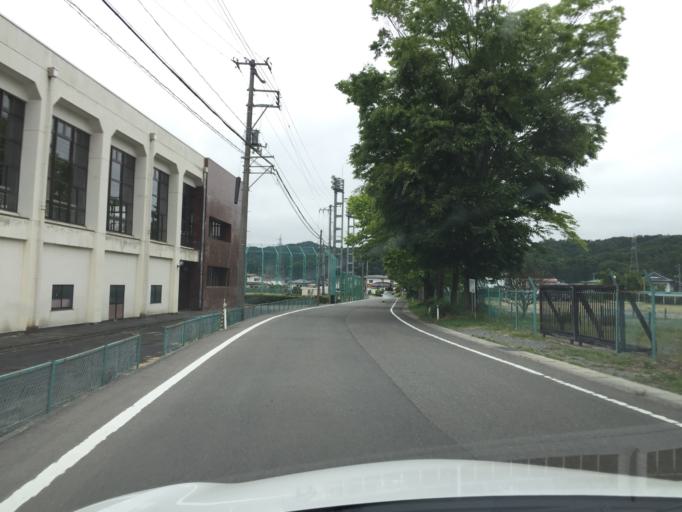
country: JP
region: Fukushima
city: Funehikimachi-funehiki
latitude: 37.3257
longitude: 140.6638
